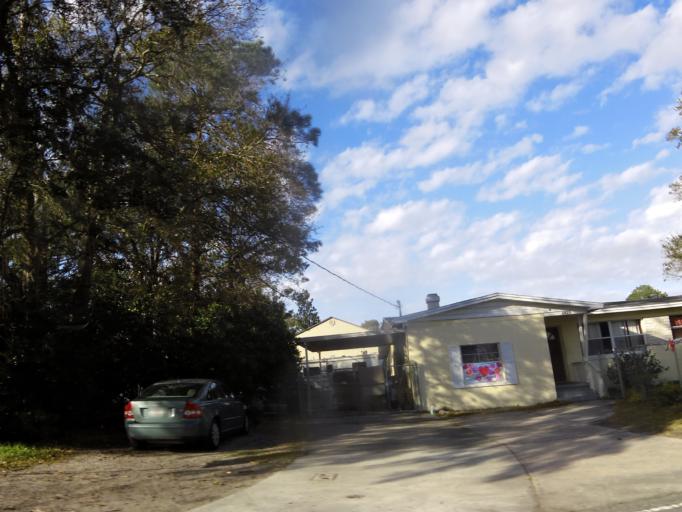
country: US
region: Florida
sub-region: Duval County
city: Jacksonville
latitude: 30.2773
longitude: -81.5962
